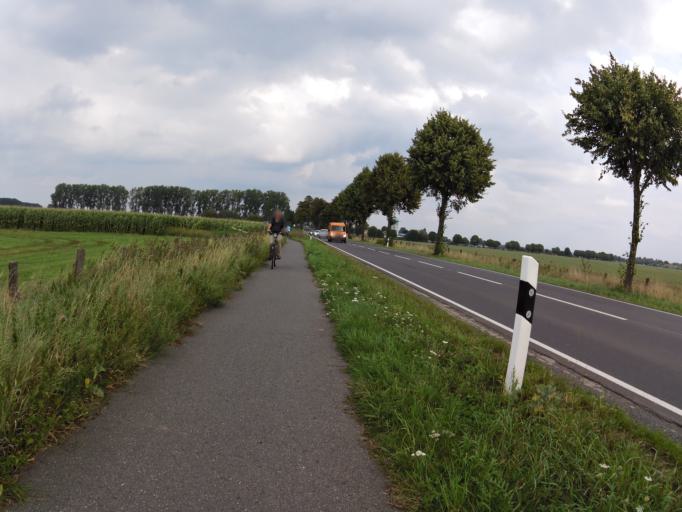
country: DE
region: Lower Saxony
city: Blender
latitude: 52.9229
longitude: 9.1700
